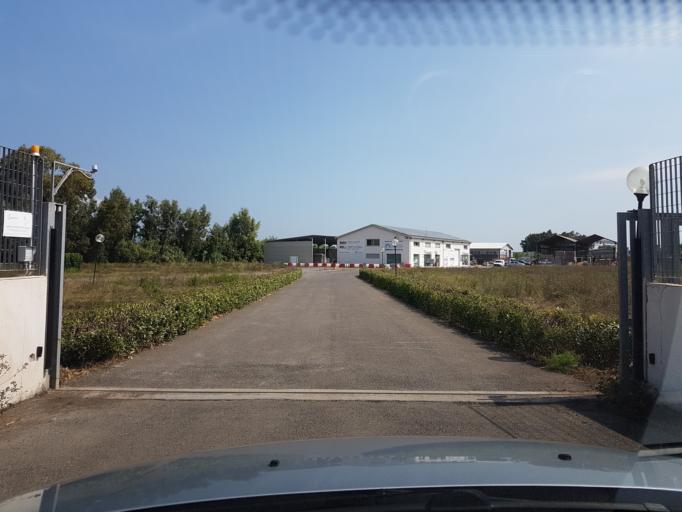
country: IT
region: Sardinia
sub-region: Provincia di Oristano
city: Donigala Fenugheddu
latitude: 39.9464
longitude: 8.5660
